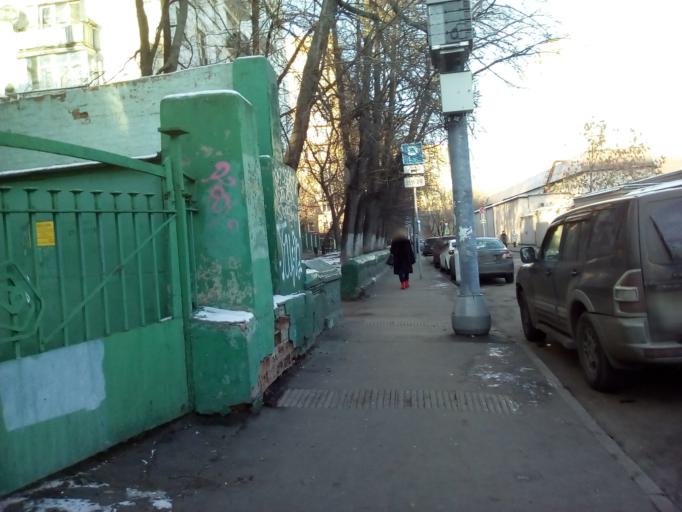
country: RU
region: Moskovskaya
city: Dorogomilovo
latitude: 55.7638
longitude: 37.5740
